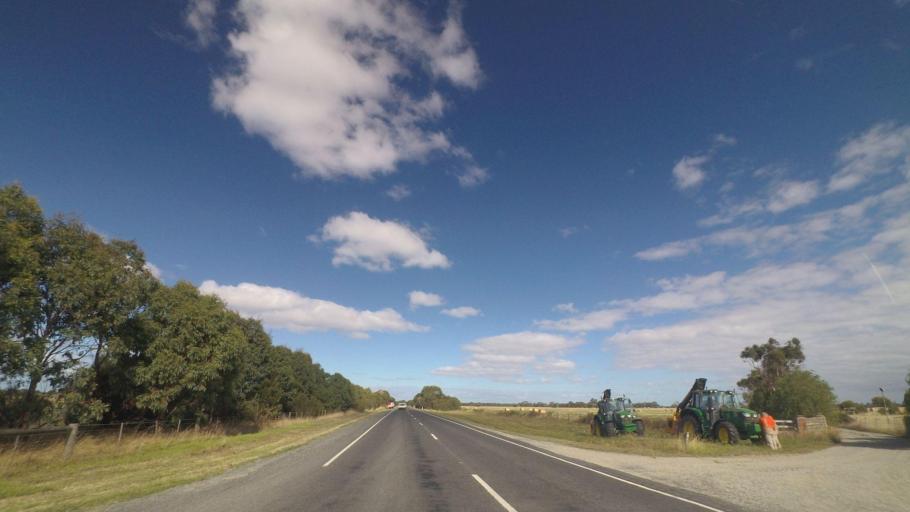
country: AU
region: Victoria
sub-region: Cardinia
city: Koo-Wee-Rup
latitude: -38.1856
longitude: 145.5436
